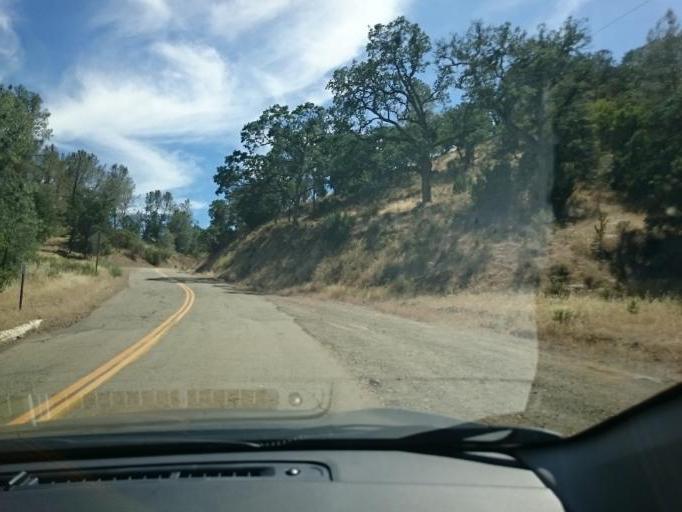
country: US
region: California
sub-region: Stanislaus County
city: Patterson
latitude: 37.3930
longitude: -121.4496
